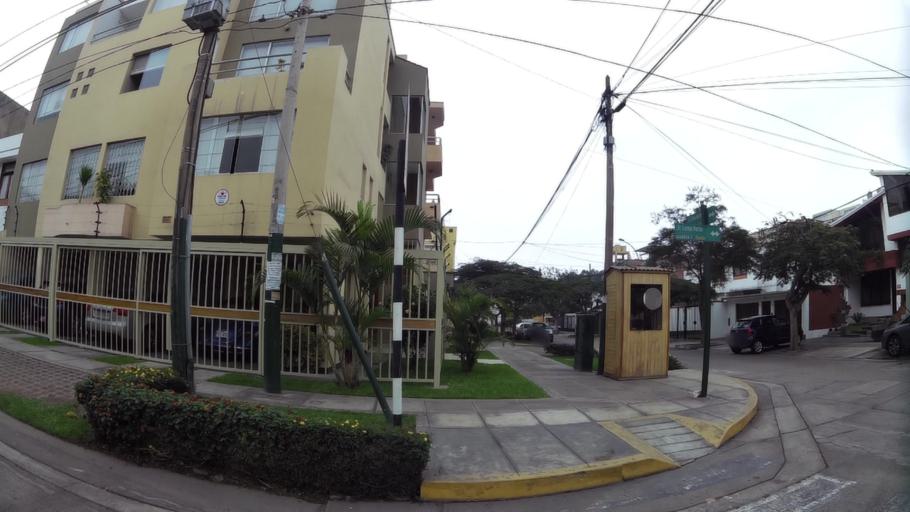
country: PE
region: Lima
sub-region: Lima
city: Surco
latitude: -12.1382
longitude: -76.9904
